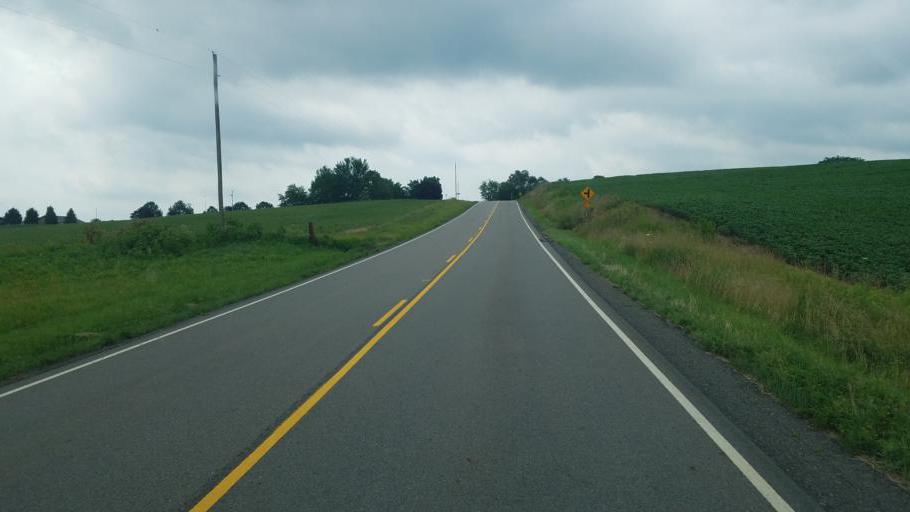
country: US
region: Ohio
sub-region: Licking County
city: Utica
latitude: 40.2199
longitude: -82.5191
